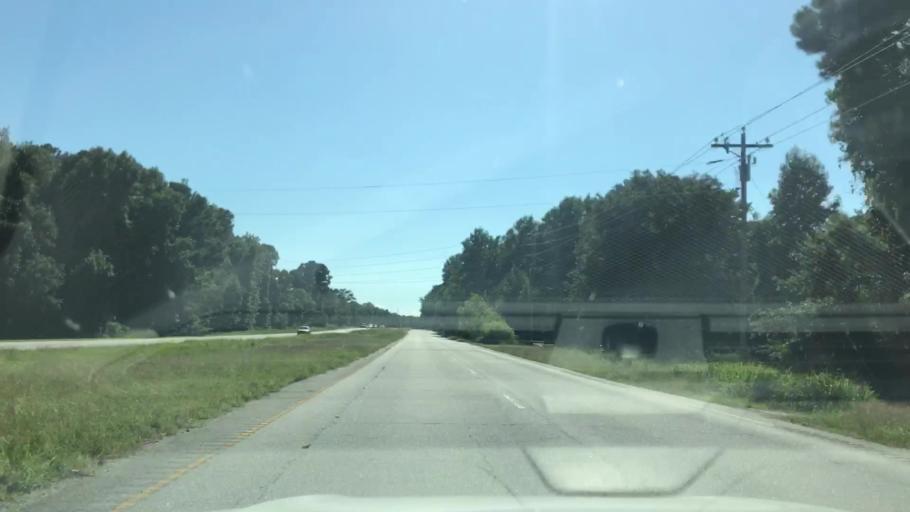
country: US
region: South Carolina
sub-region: Charleston County
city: Awendaw
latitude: 33.0513
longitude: -79.5559
